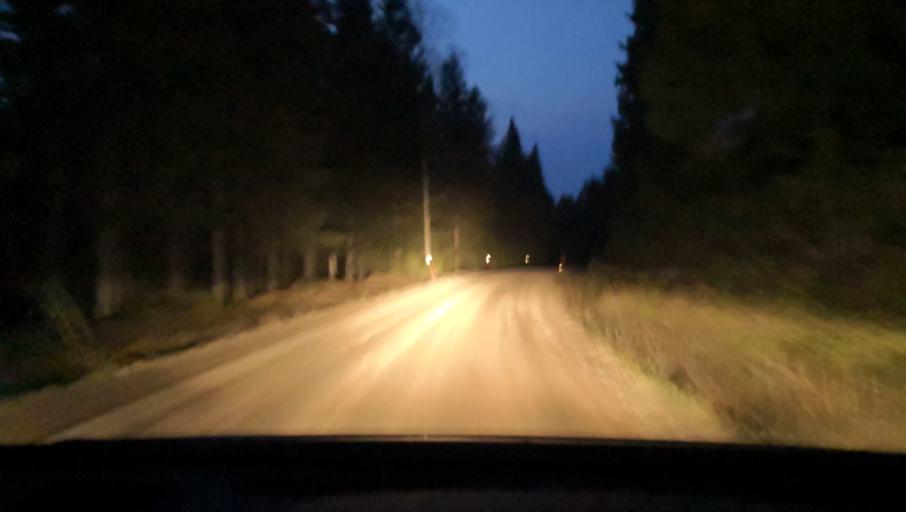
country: SE
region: OErebro
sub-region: Lindesbergs Kommun
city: Frovi
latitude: 59.6293
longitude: 15.4734
